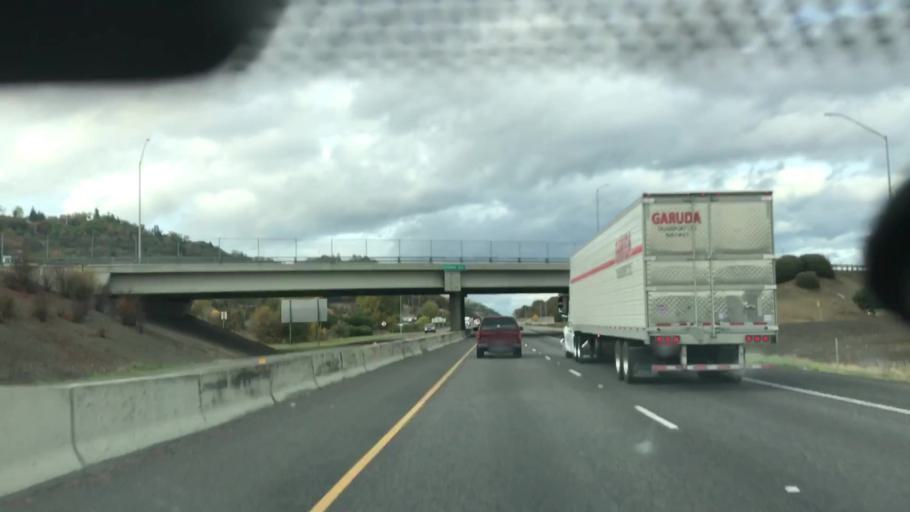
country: US
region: Oregon
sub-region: Douglas County
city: Roseburg
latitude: 43.2469
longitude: -123.3601
